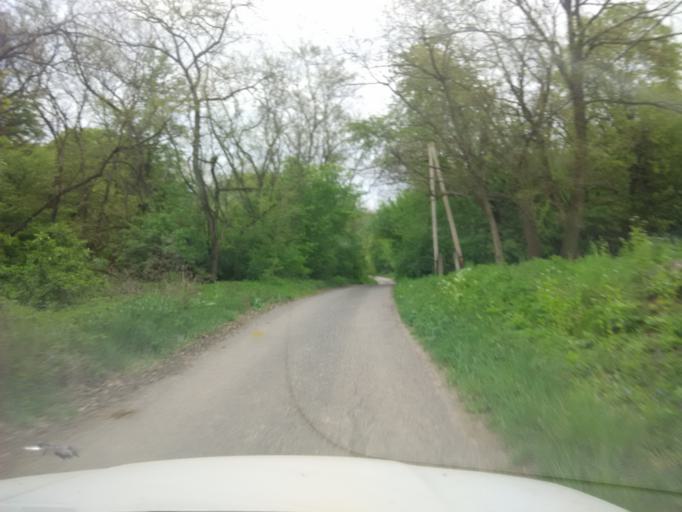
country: SK
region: Nitriansky
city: Levice
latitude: 48.2848
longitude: 18.7039
